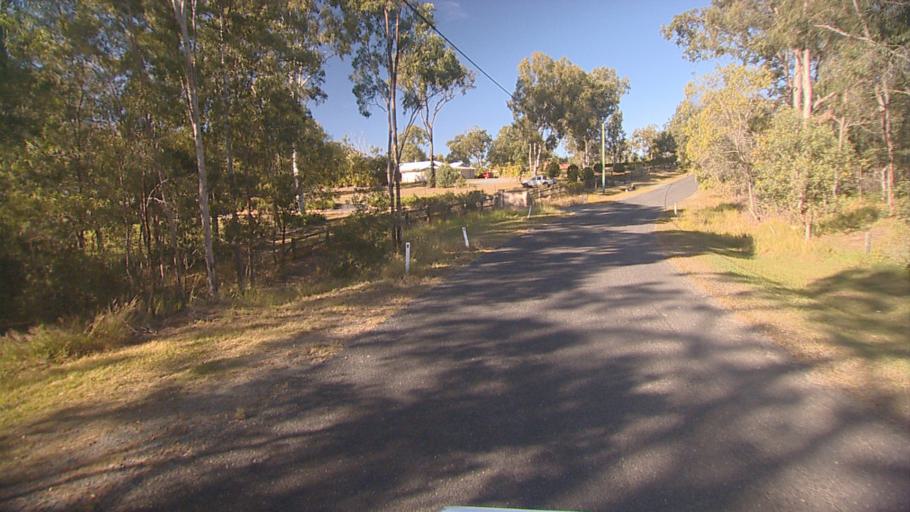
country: AU
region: Queensland
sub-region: Ipswich
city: Springfield Lakes
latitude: -27.7030
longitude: 152.9312
